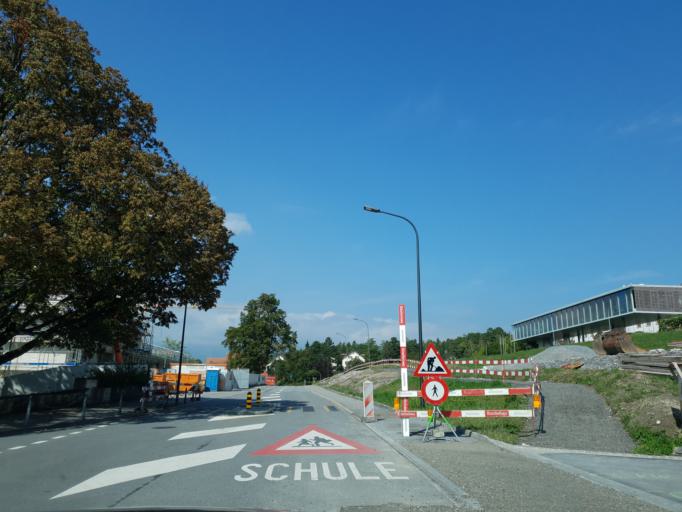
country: LI
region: Vaduz
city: Vaduz
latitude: 47.1482
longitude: 9.5158
